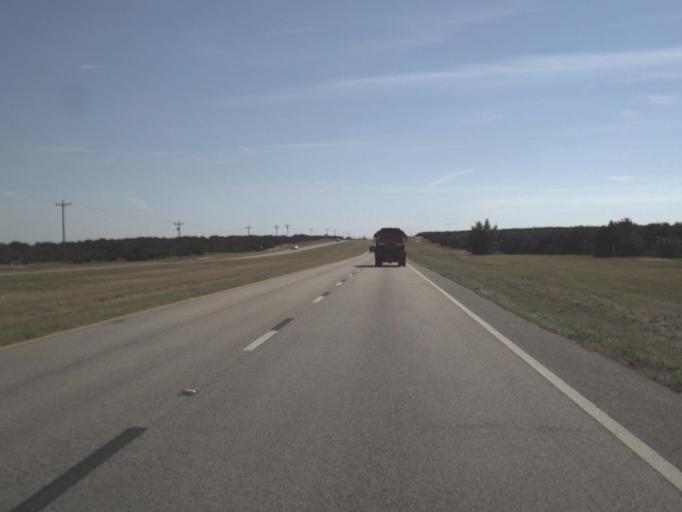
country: US
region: Florida
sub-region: Highlands County
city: Placid Lakes
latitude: 27.1908
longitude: -81.3288
